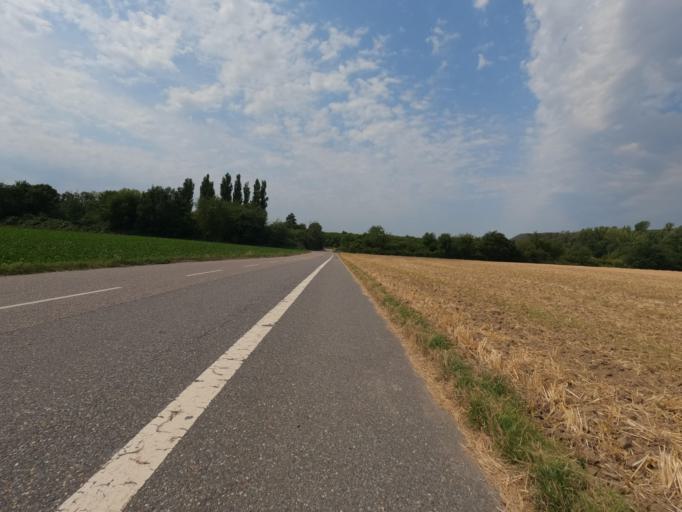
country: DE
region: North Rhine-Westphalia
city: Siersdorf
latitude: 50.9148
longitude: 6.2345
